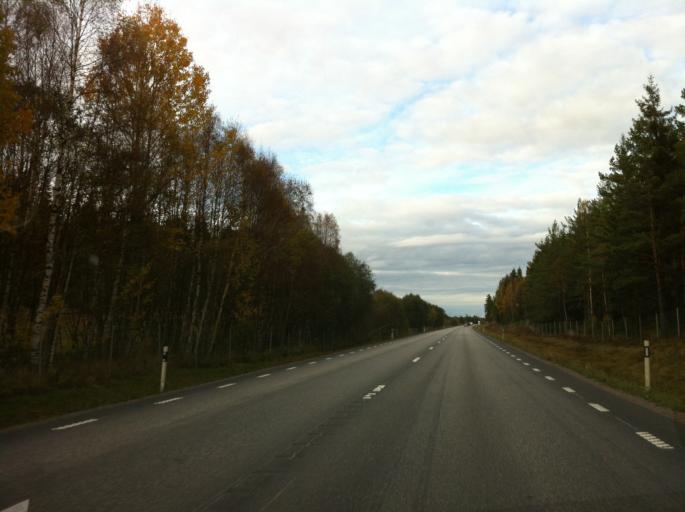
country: SE
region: OErebro
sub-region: Askersunds Kommun
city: Asbro
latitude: 58.9579
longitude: 15.0333
